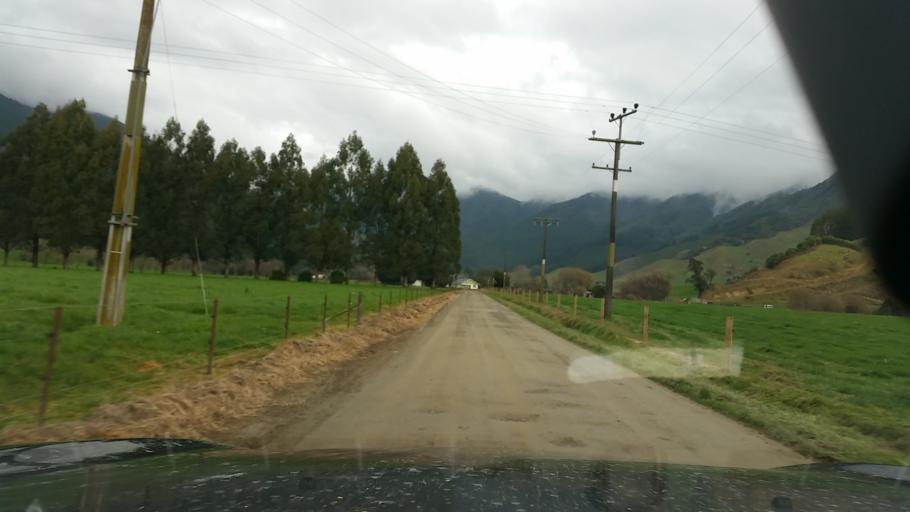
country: NZ
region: Marlborough
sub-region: Marlborough District
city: Picton
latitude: -41.2900
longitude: 173.8587
